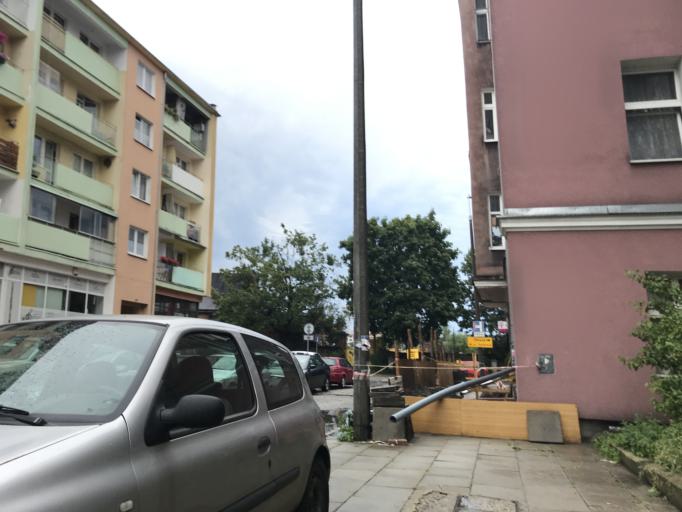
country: PL
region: Pomeranian Voivodeship
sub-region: Gdansk
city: Gdansk
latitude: 54.3503
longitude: 18.6661
